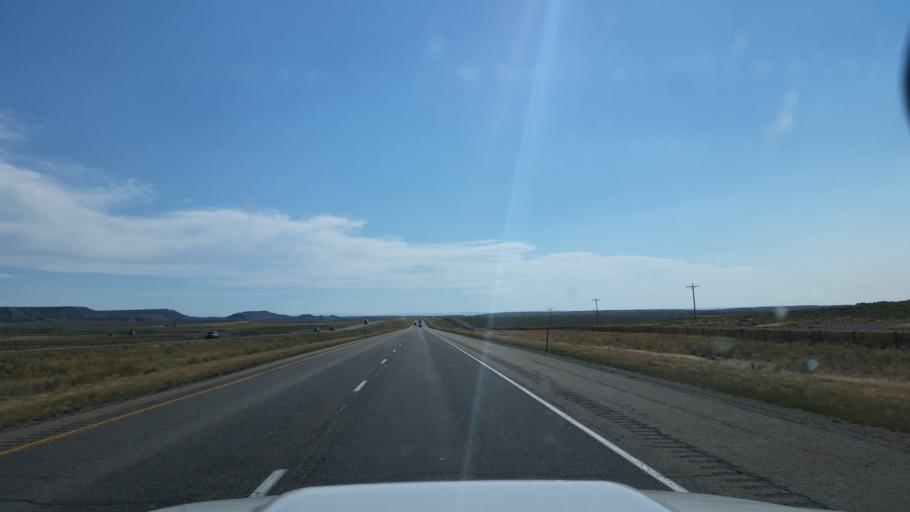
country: US
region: Wyoming
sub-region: Uinta County
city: Lyman
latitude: 41.4538
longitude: -110.0687
